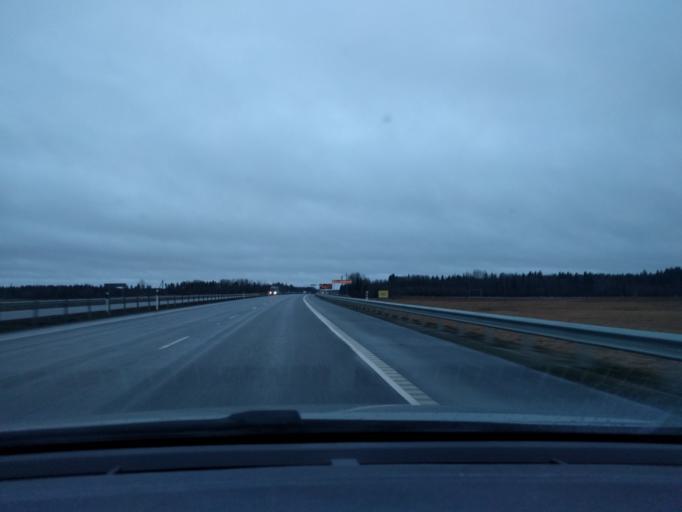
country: EE
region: Harju
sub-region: Rae vald
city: Vaida
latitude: 59.2371
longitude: 25.0292
